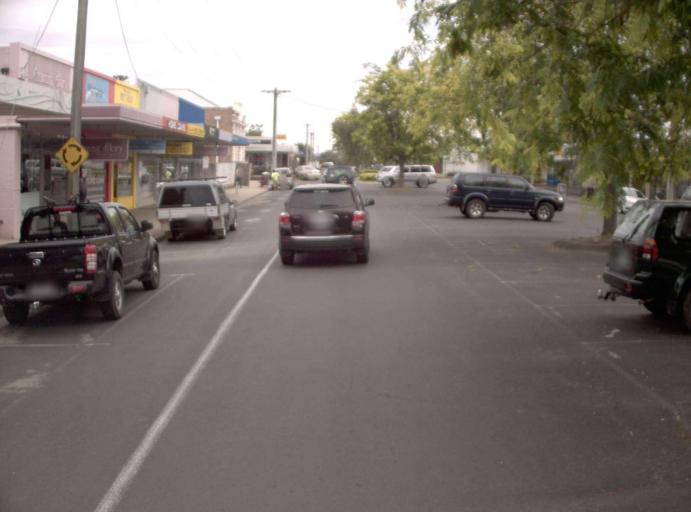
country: AU
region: Victoria
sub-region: East Gippsland
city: Bairnsdale
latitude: -37.8260
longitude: 147.6292
